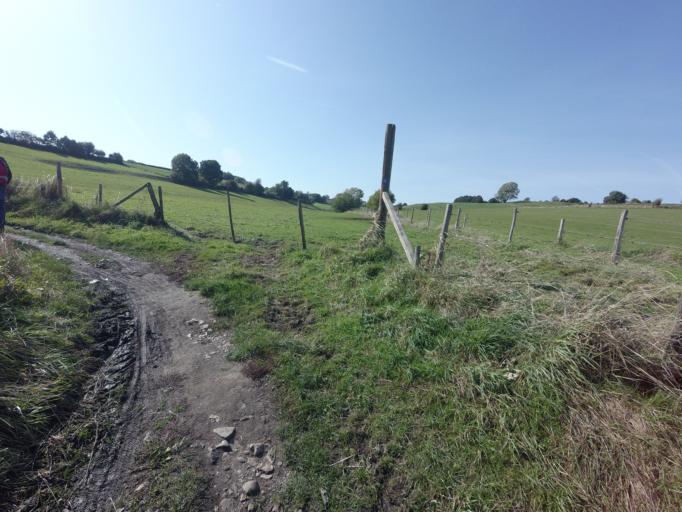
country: BE
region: Wallonia
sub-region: Province de Liege
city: Plombieres
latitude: 50.7817
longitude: 5.9068
